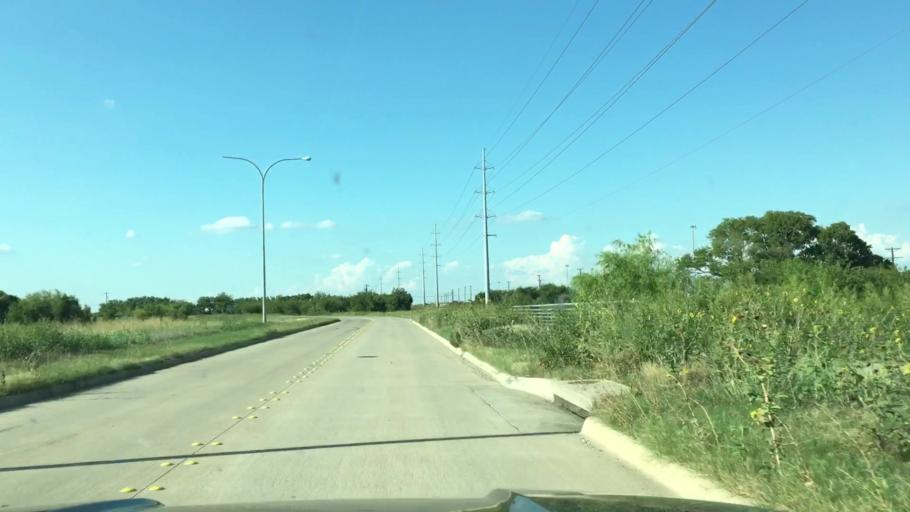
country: US
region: Texas
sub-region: Tarrant County
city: Haslet
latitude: 33.0107
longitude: -97.3558
